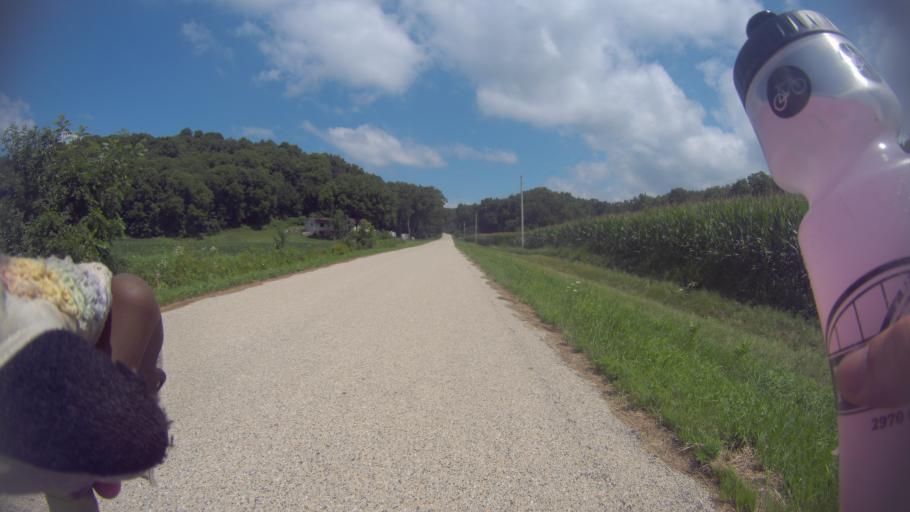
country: US
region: Wisconsin
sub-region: Sauk County
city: Sauk City
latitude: 43.2221
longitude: -89.6206
